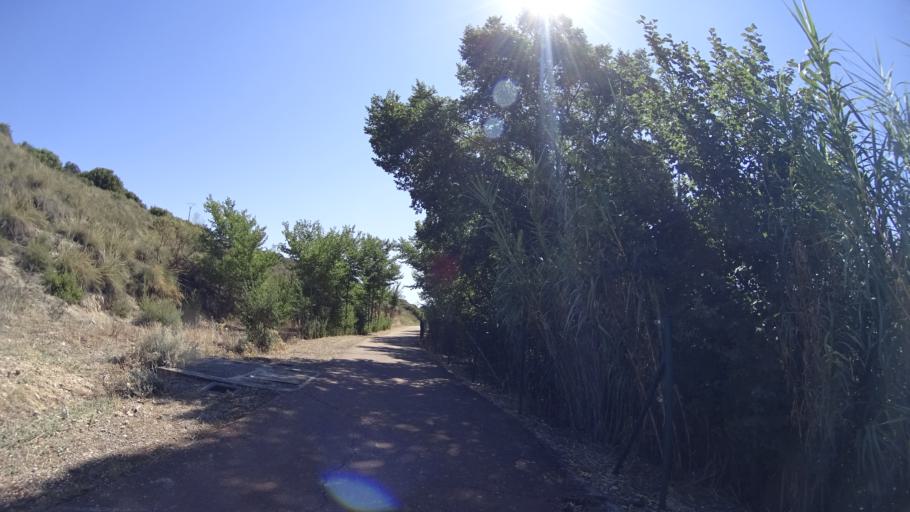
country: ES
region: Madrid
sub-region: Provincia de Madrid
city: Morata de Tajuna
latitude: 40.2310
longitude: -3.4042
